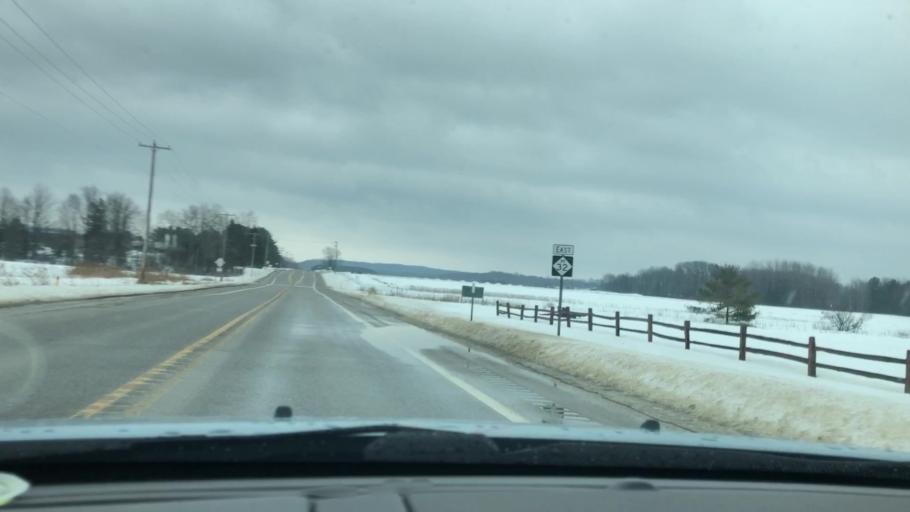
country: US
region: Michigan
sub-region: Charlevoix County
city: East Jordan
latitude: 45.1325
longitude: -85.1179
